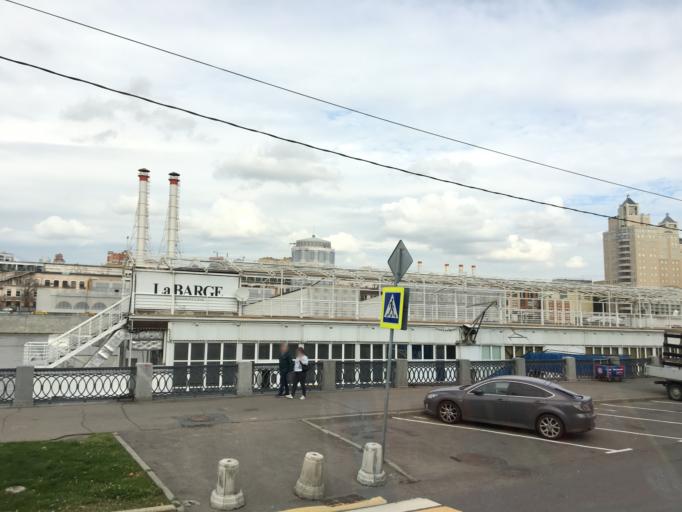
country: RU
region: Moskovskaya
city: Dorogomilovo
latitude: 55.7524
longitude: 37.5624
